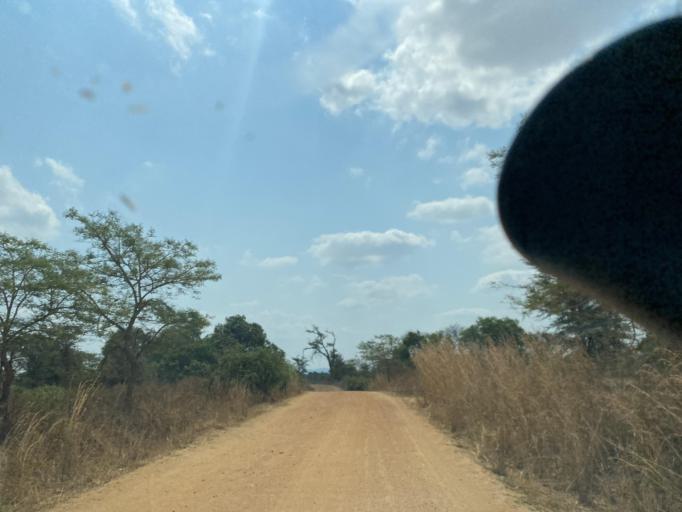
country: ZM
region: Lusaka
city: Chongwe
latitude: -15.5869
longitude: 28.7644
